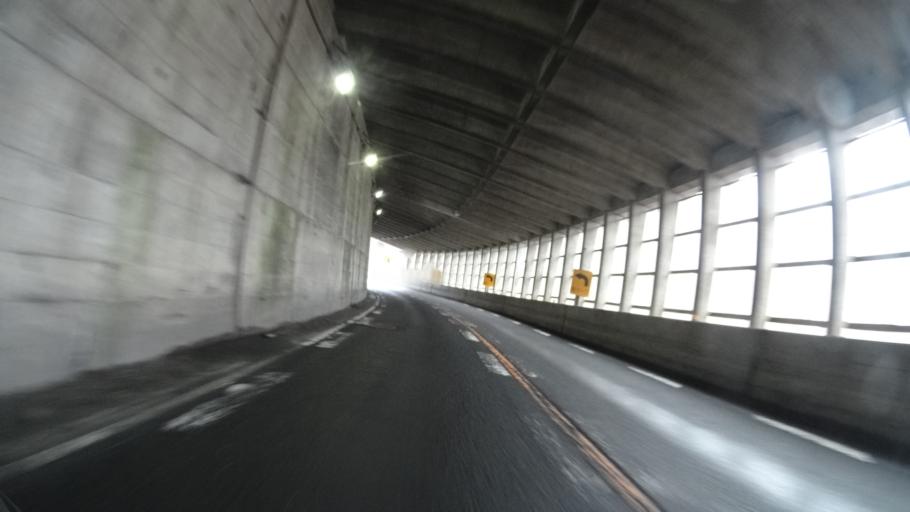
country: JP
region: Gunma
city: Nakanojomachi
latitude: 36.7507
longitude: 138.8344
